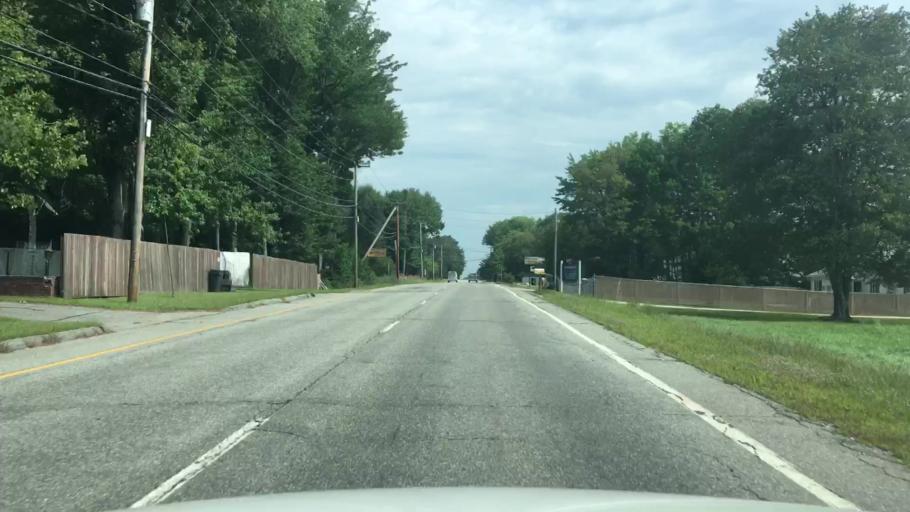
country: US
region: Maine
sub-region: Androscoggin County
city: Auburn
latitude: 44.0633
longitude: -70.2502
